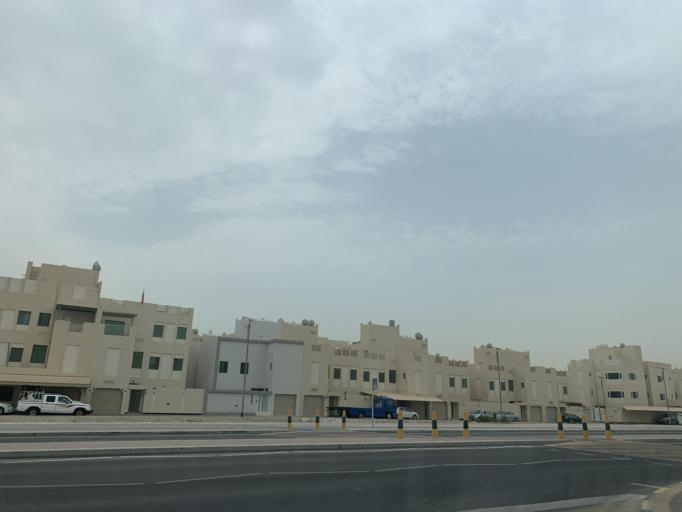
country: BH
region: Northern
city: Madinat `Isa
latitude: 26.1777
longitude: 50.5152
